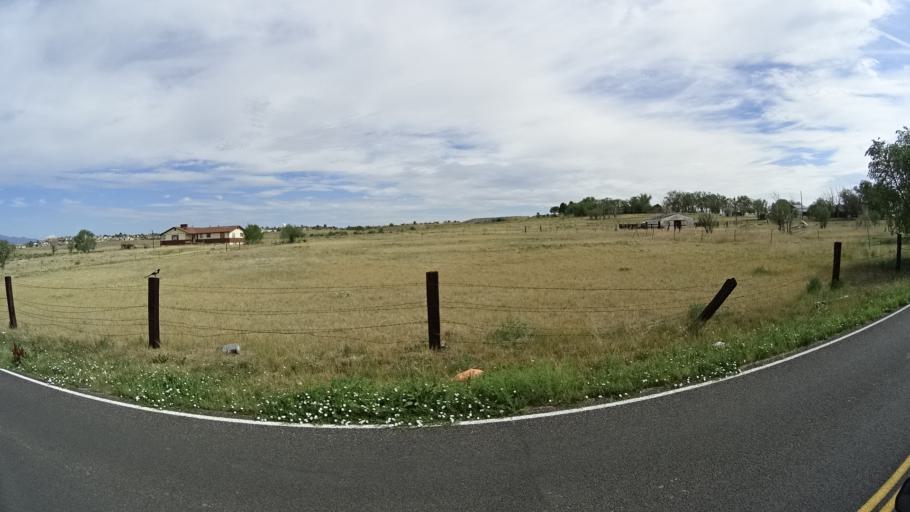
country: US
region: Colorado
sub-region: El Paso County
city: Fountain
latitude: 38.7084
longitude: -104.6785
